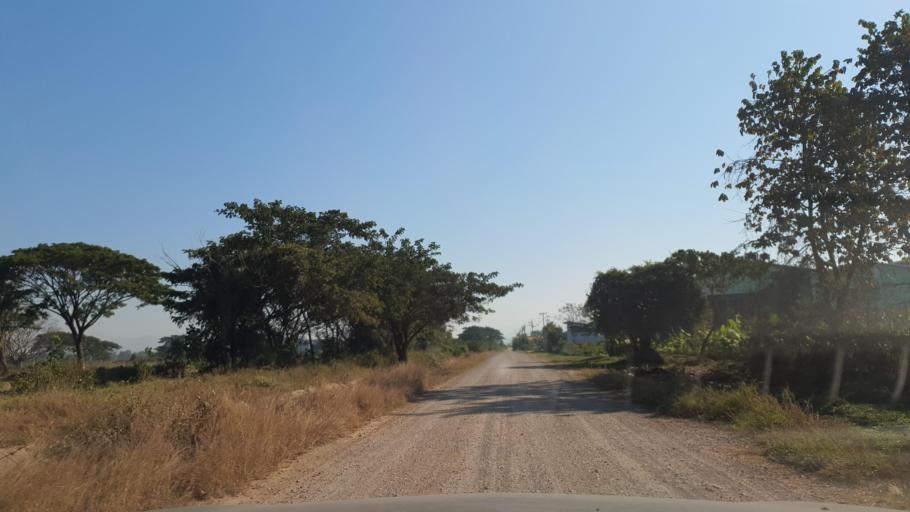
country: TH
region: Chiang Mai
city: San Kamphaeng
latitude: 18.7045
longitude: 99.1375
